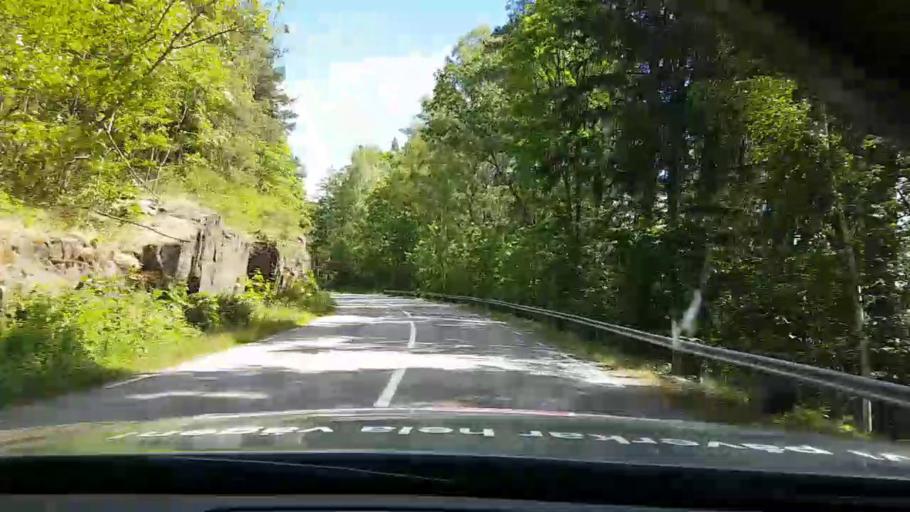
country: SE
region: Kalmar
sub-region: Vasterviks Kommun
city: Overum
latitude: 58.0715
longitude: 16.3755
